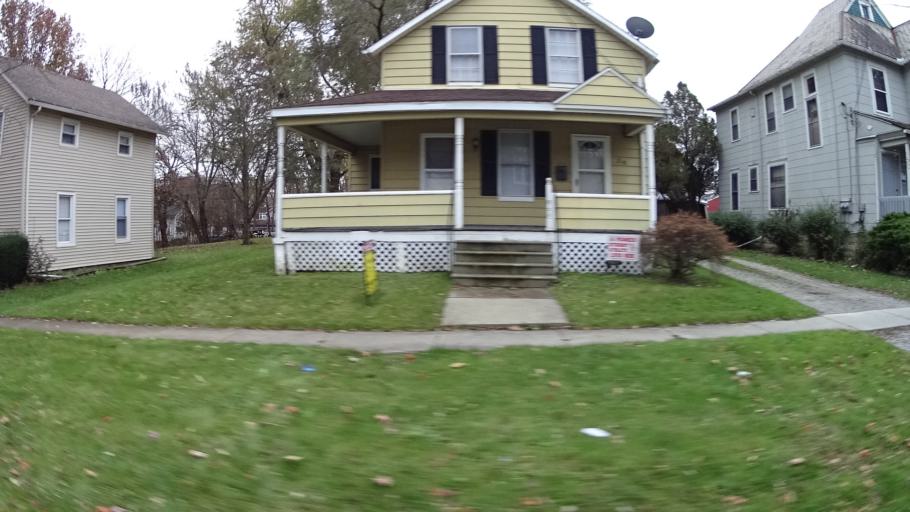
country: US
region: Ohio
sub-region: Lorain County
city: Elyria
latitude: 41.3598
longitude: -82.1051
